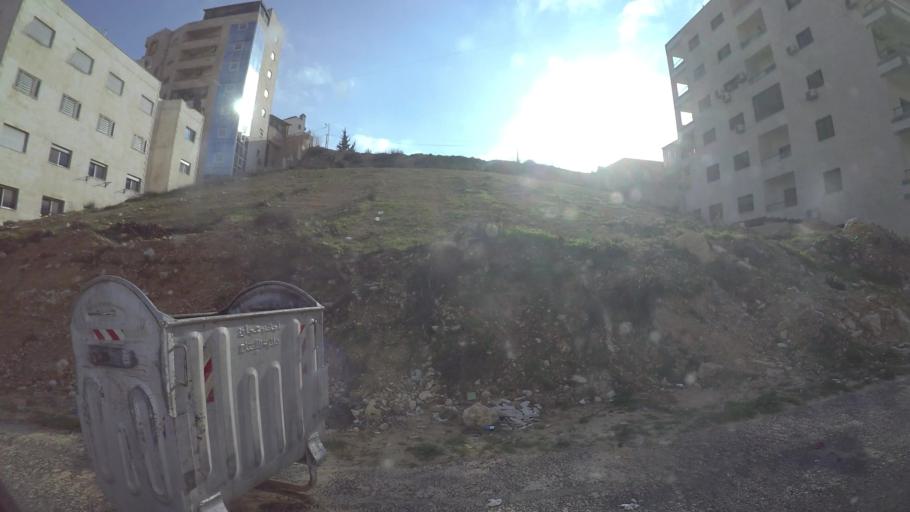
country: JO
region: Amman
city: Al Jubayhah
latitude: 32.0087
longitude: 35.8603
